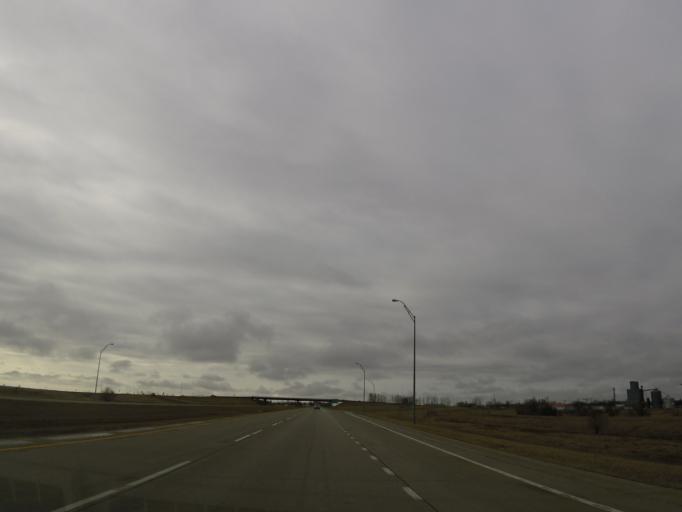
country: US
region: North Dakota
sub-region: Grand Forks County
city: Grand Forks
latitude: 48.0818
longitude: -97.1695
